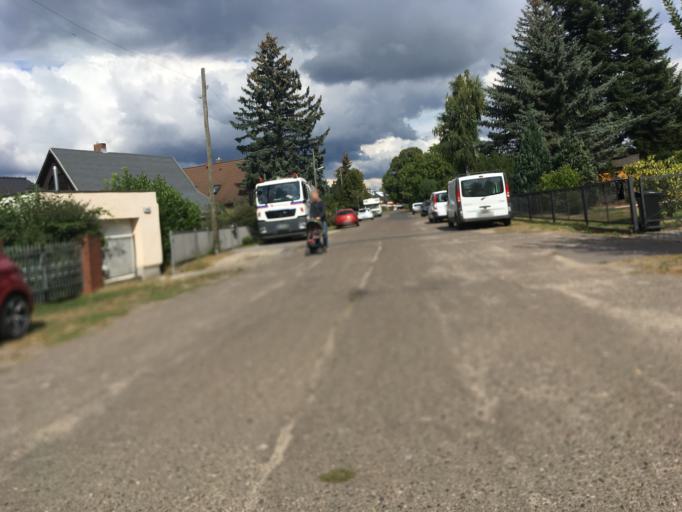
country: DE
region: Berlin
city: Karow
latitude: 52.6082
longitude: 13.4965
